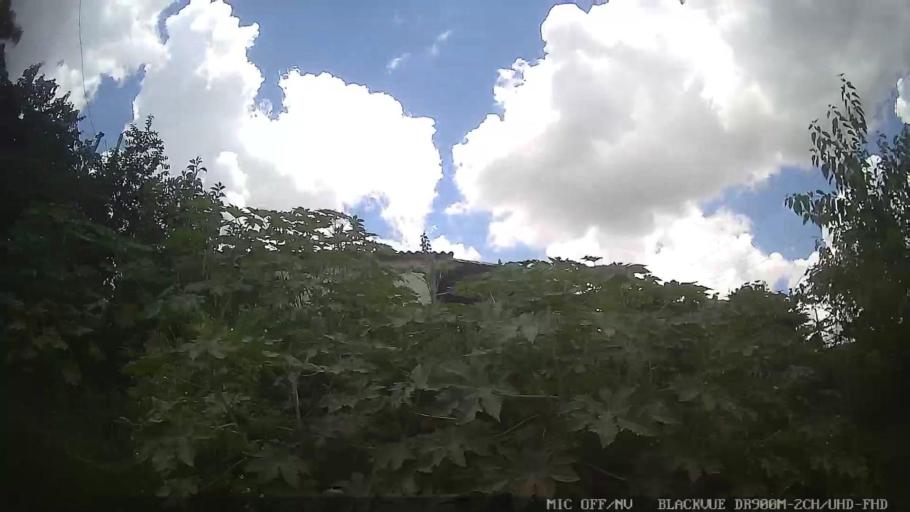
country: BR
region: Sao Paulo
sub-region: Atibaia
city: Atibaia
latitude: -23.1209
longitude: -46.6189
